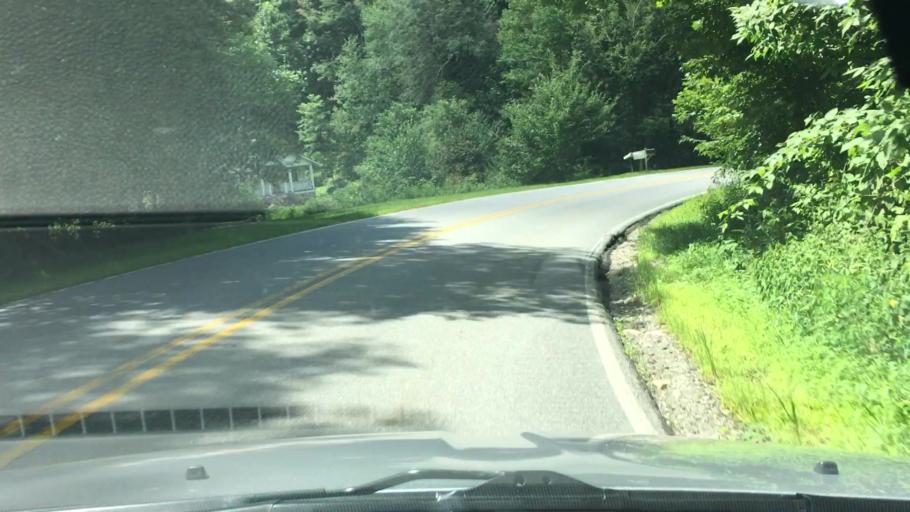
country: US
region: North Carolina
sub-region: Madison County
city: Mars Hill
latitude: 35.9201
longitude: -82.5315
